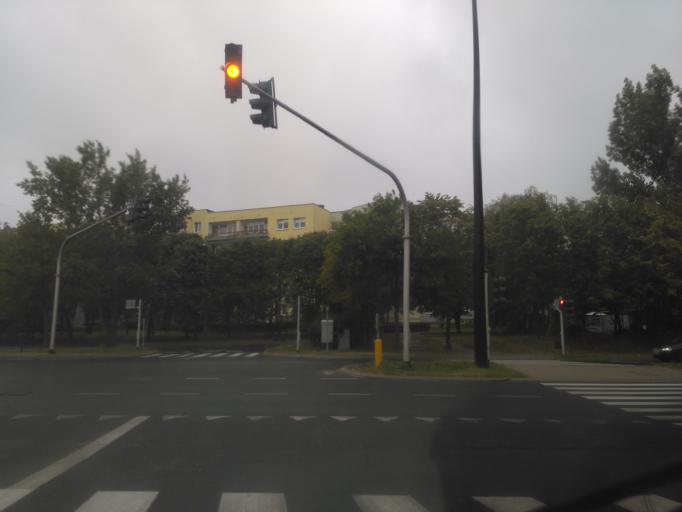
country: PL
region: Lublin Voivodeship
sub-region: Powiat lubelski
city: Lublin
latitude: 51.2675
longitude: 22.5585
